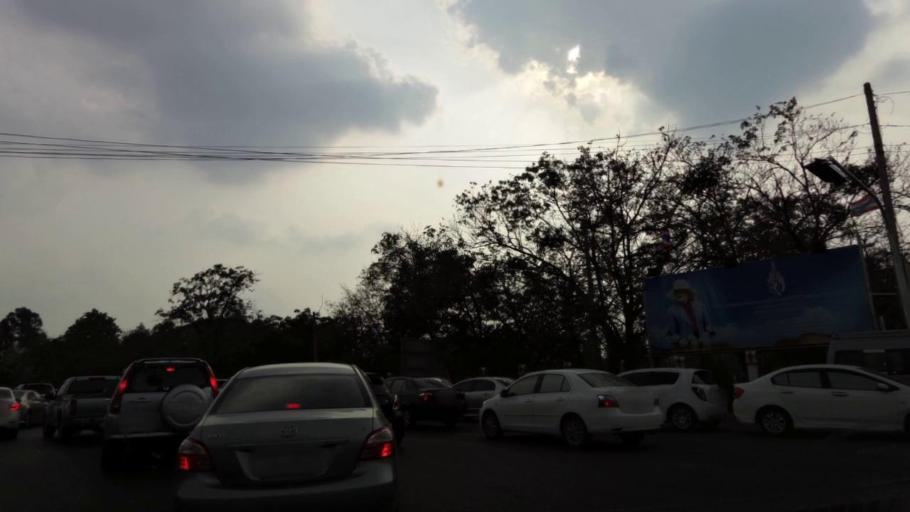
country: TH
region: Phra Nakhon Si Ayutthaya
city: Phra Nakhon Si Ayutthaya
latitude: 14.3763
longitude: 100.5410
